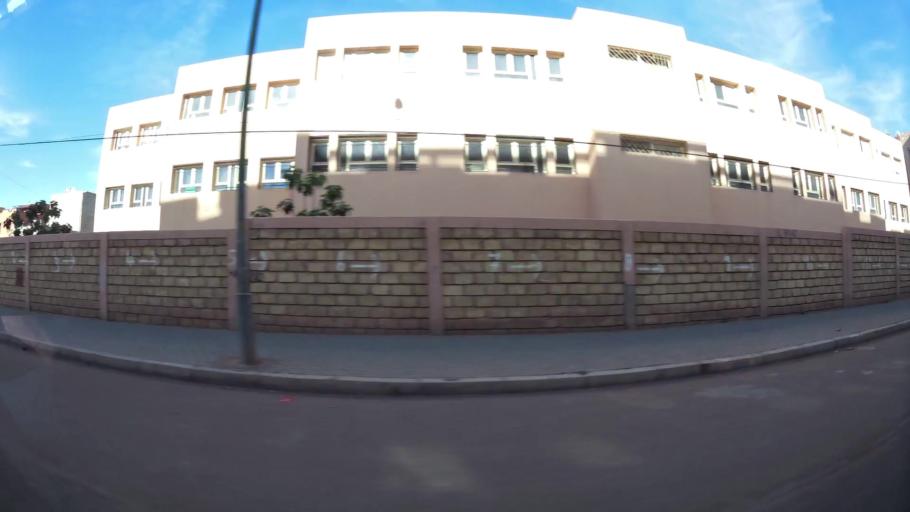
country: MA
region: Marrakech-Tensift-Al Haouz
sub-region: Marrakech
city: Marrakesh
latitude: 31.6870
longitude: -8.0642
